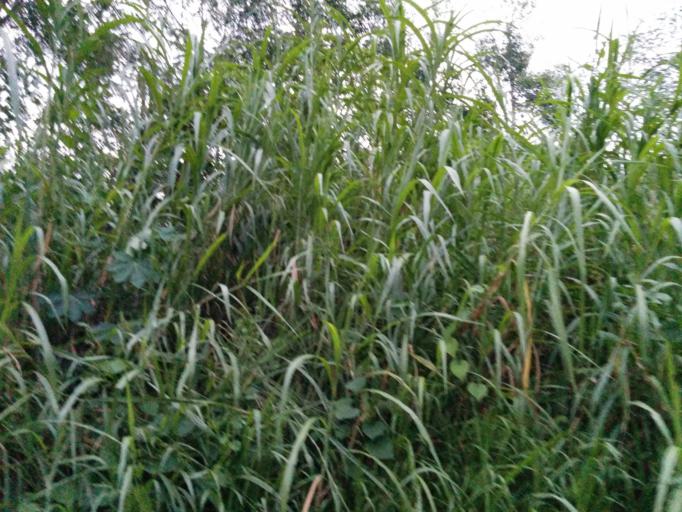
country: MY
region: Johor
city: Kampung Pasir Gudang Baru
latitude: 1.4003
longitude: 103.8804
